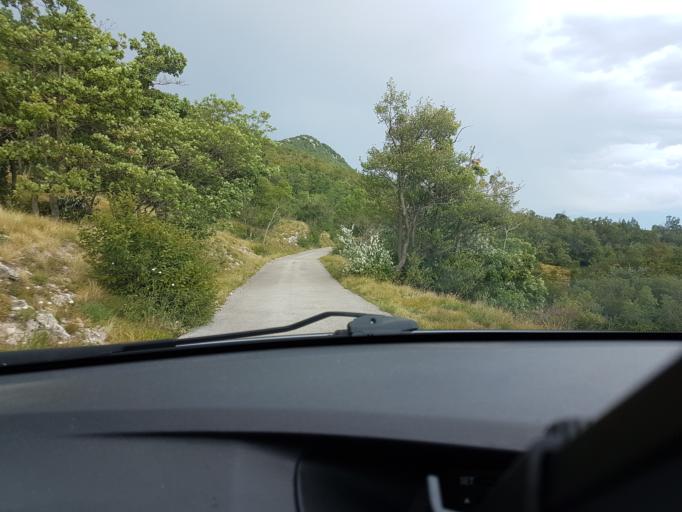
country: HR
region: Primorsko-Goranska
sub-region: Grad Crikvenica
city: Crikvenica
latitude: 45.2369
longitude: 14.6969
